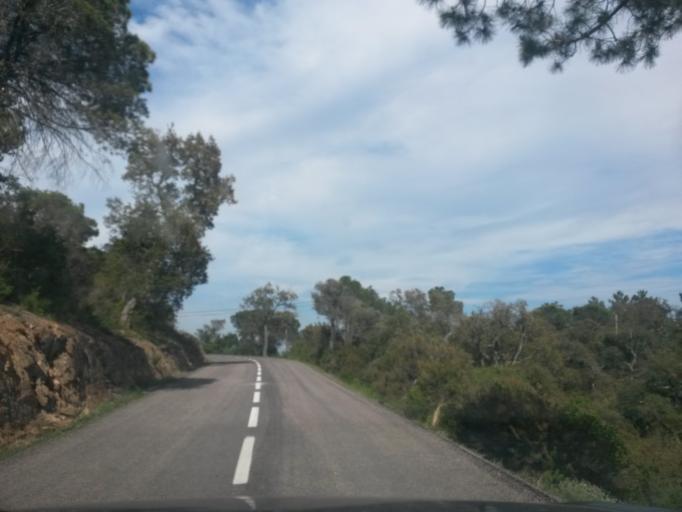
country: ES
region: Catalonia
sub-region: Provincia de Girona
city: Brunyola
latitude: 41.9002
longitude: 2.6810
